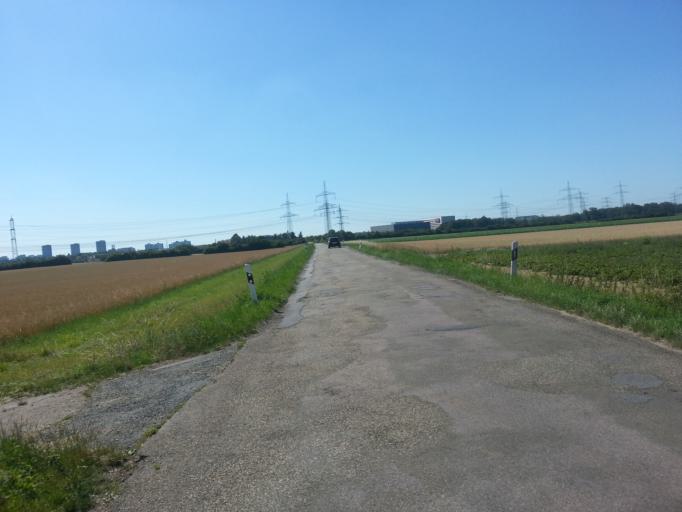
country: DE
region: Hesse
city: Viernheim
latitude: 49.5097
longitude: 8.5718
